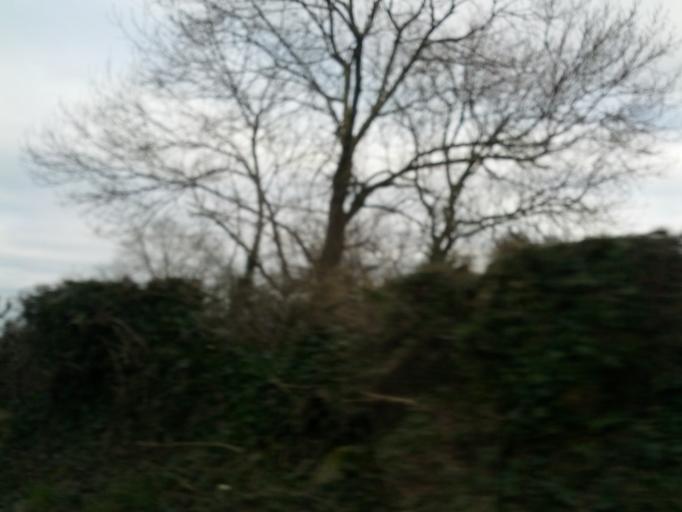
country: IE
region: Connaught
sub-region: County Galway
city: Gort
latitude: 53.1738
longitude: -8.8475
